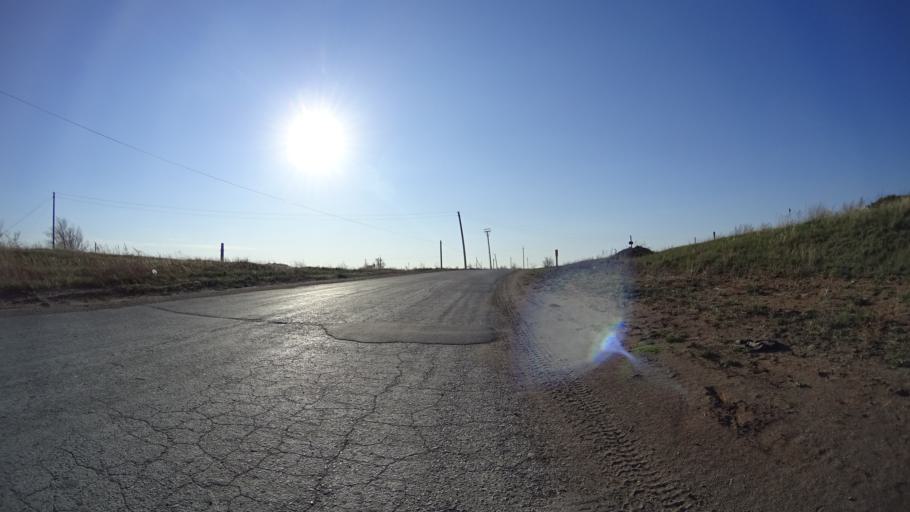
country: RU
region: Chelyabinsk
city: Troitsk
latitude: 54.0770
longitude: 61.6016
